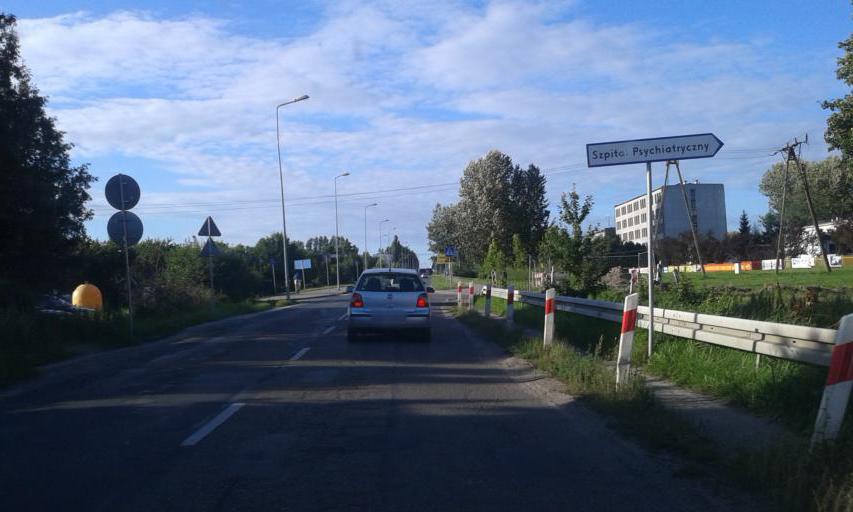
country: PL
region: West Pomeranian Voivodeship
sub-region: Koszalin
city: Koszalin
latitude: 54.1707
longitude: 16.1843
